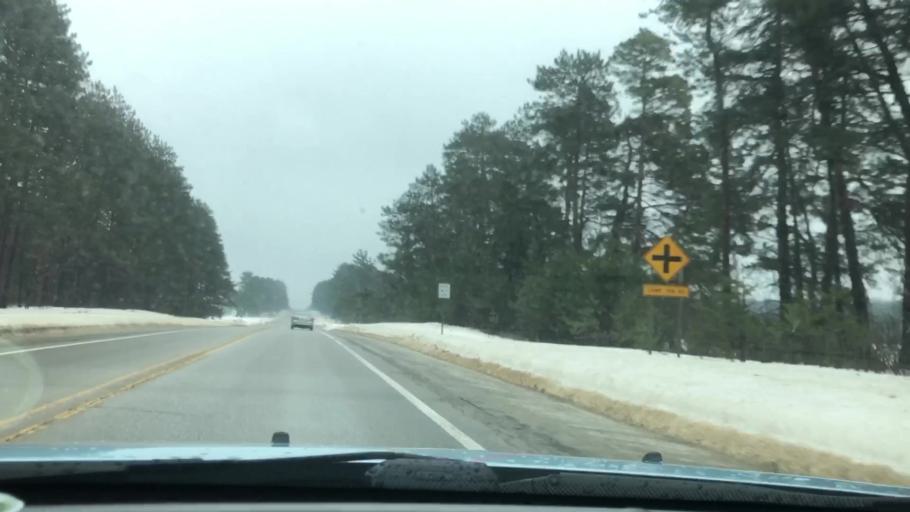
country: US
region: Michigan
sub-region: Otsego County
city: Gaylord
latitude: 45.0619
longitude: -84.8194
